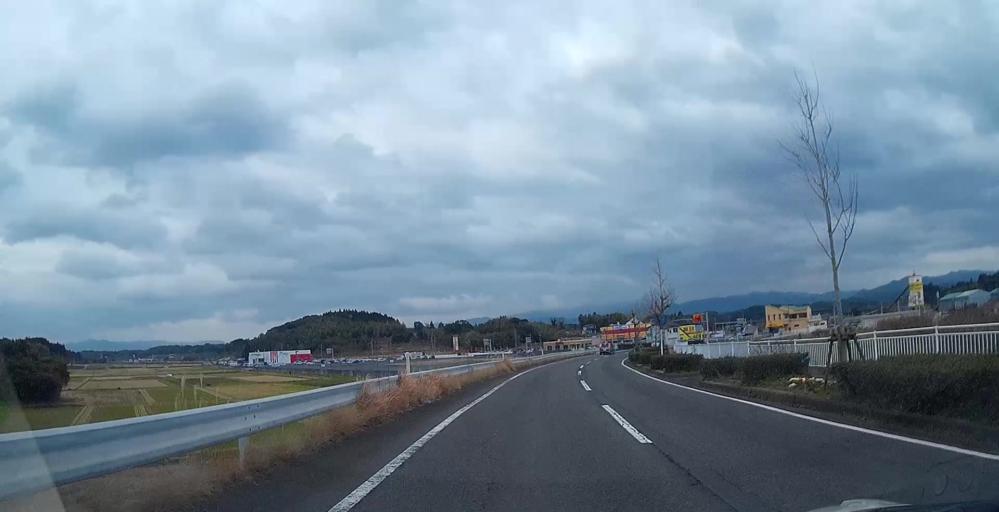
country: JP
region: Kagoshima
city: Akune
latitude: 32.0633
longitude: 130.2249
